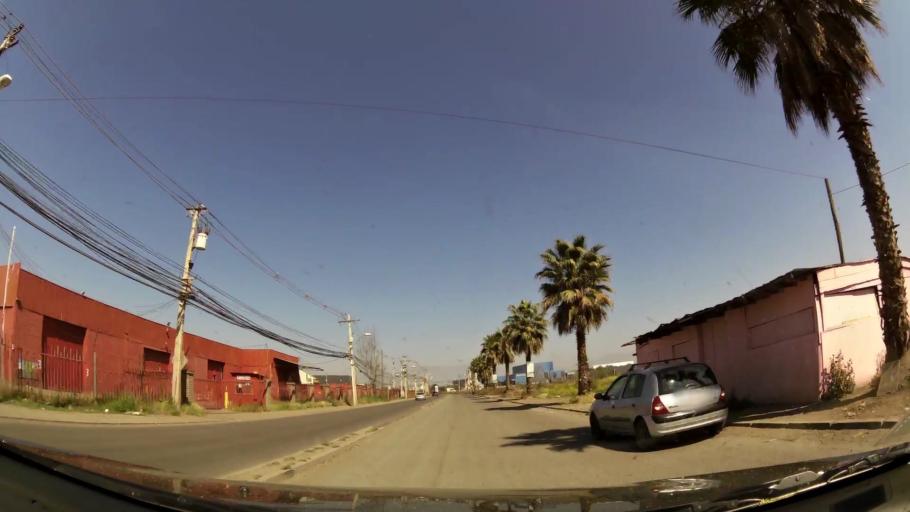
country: CL
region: Santiago Metropolitan
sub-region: Provincia de Chacabuco
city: Chicureo Abajo
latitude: -33.3139
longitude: -70.7249
